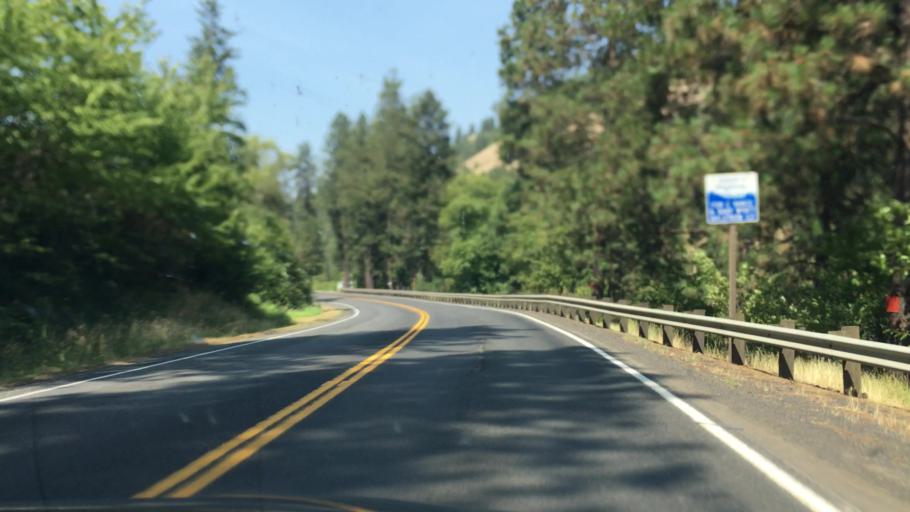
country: US
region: Idaho
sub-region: Clearwater County
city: Orofino
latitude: 46.5002
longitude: -116.3906
